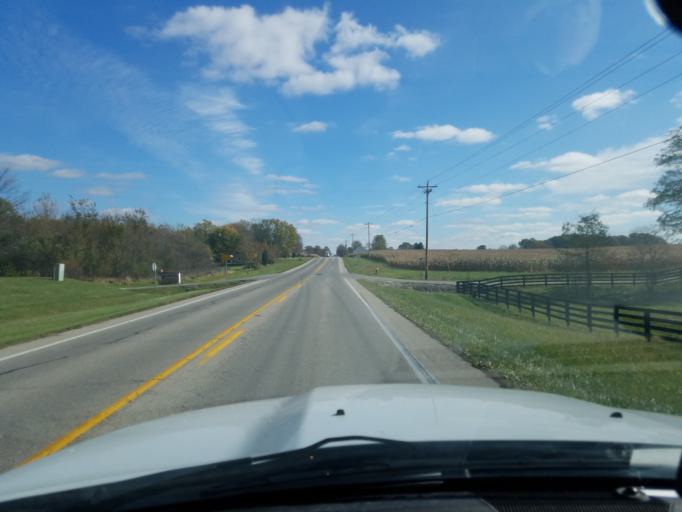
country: US
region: Indiana
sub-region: Ripley County
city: Osgood
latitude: 39.0750
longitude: -85.3162
